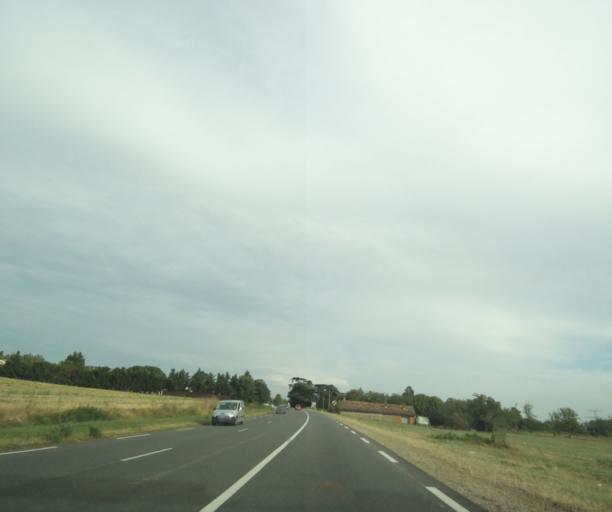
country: FR
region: Midi-Pyrenees
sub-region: Departement de la Haute-Garonne
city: Castelnau-d'Estretefonds
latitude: 43.7918
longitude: 1.3390
